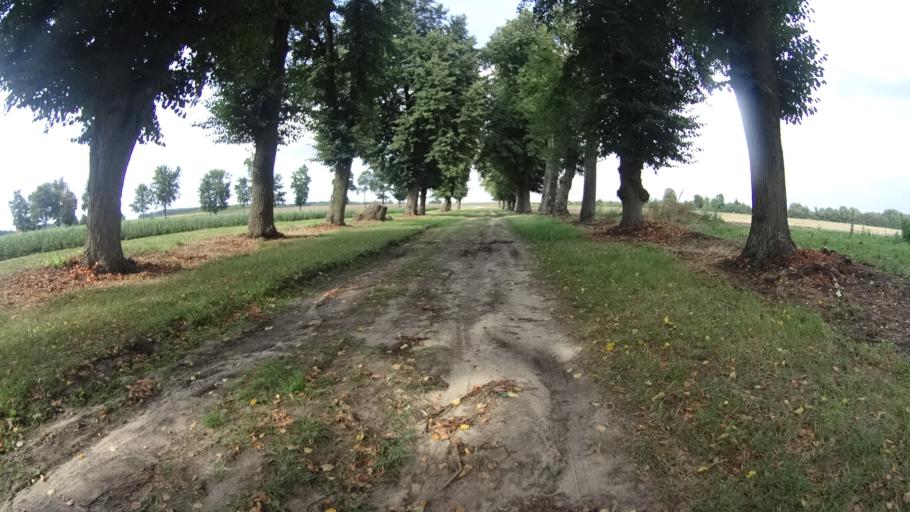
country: PL
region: Masovian Voivodeship
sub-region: Powiat grojecki
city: Goszczyn
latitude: 51.6943
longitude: 20.8236
